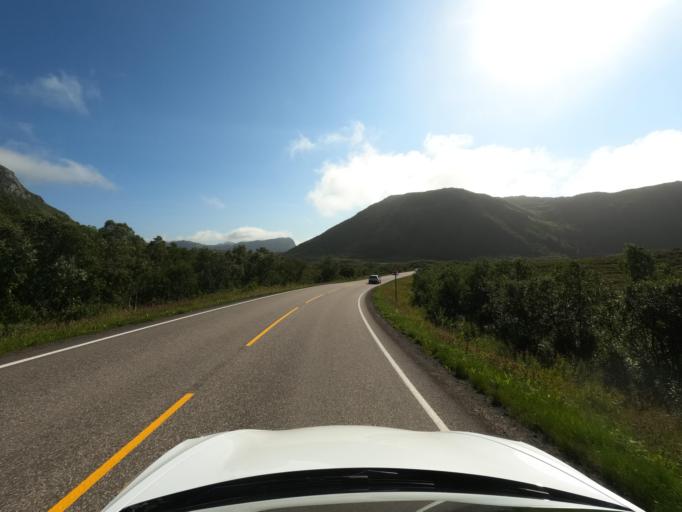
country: NO
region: Nordland
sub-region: Vestvagoy
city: Evjen
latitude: 68.2786
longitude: 13.8385
